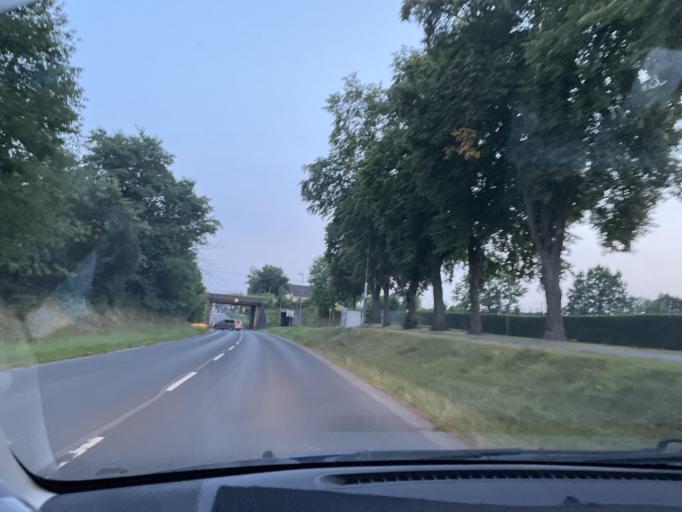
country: DE
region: Lower Saxony
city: Holzminden
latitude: 51.8319
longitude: 9.4680
